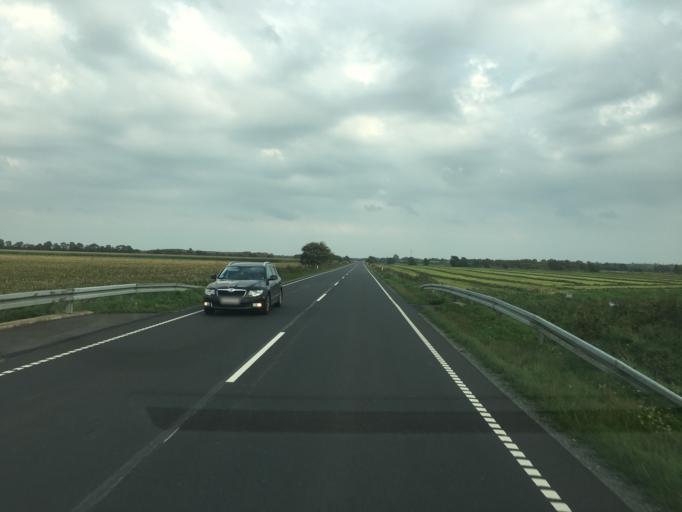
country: DE
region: Schleswig-Holstein
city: Bramstedtlund
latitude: 54.9744
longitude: 9.0567
